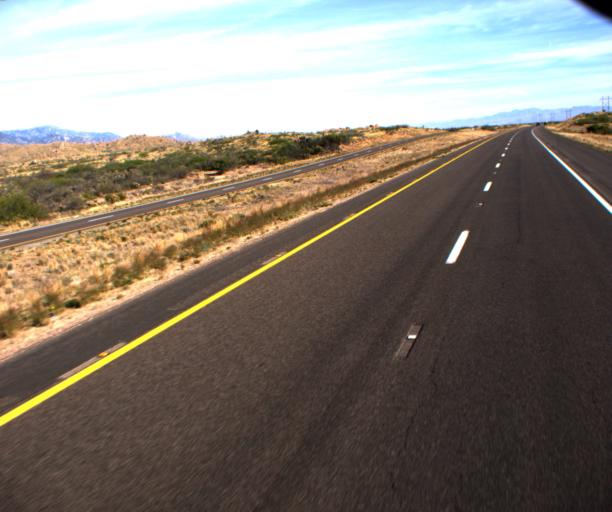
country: US
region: Arizona
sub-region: Graham County
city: Swift Trail Junction
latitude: 32.5143
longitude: -109.6738
